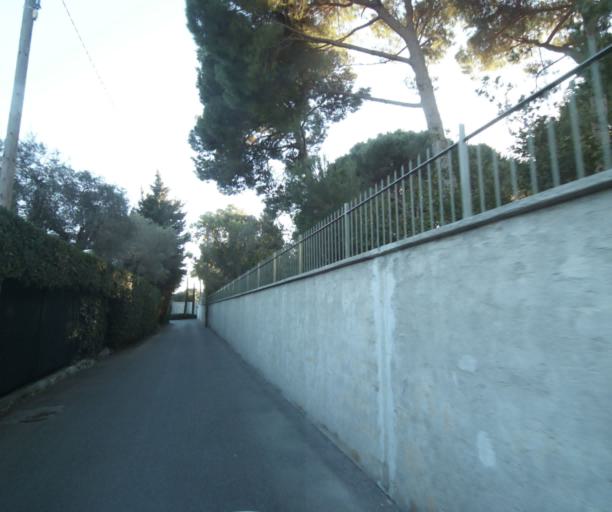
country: FR
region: Provence-Alpes-Cote d'Azur
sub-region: Departement des Alpes-Maritimes
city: Antibes
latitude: 43.5487
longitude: 7.1320
